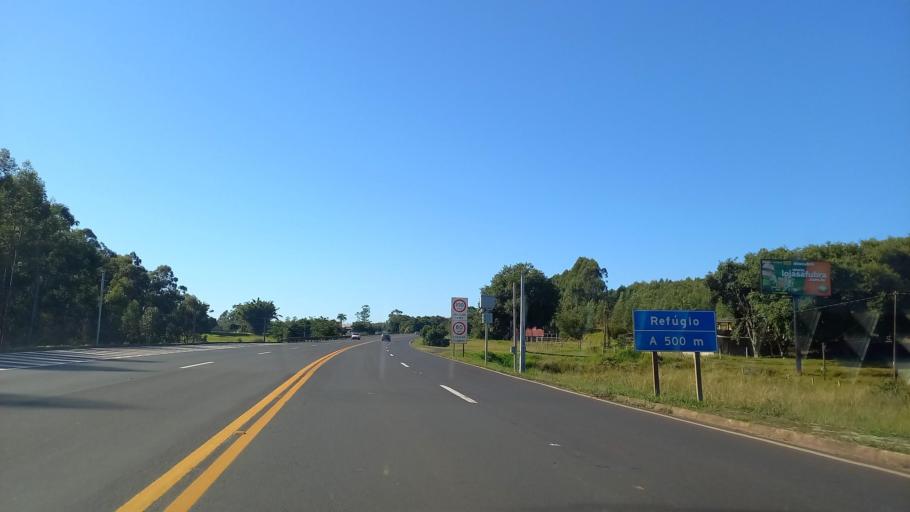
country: BR
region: Rio Grande do Sul
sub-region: Montenegro
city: Montenegro
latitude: -29.7801
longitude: -51.5532
